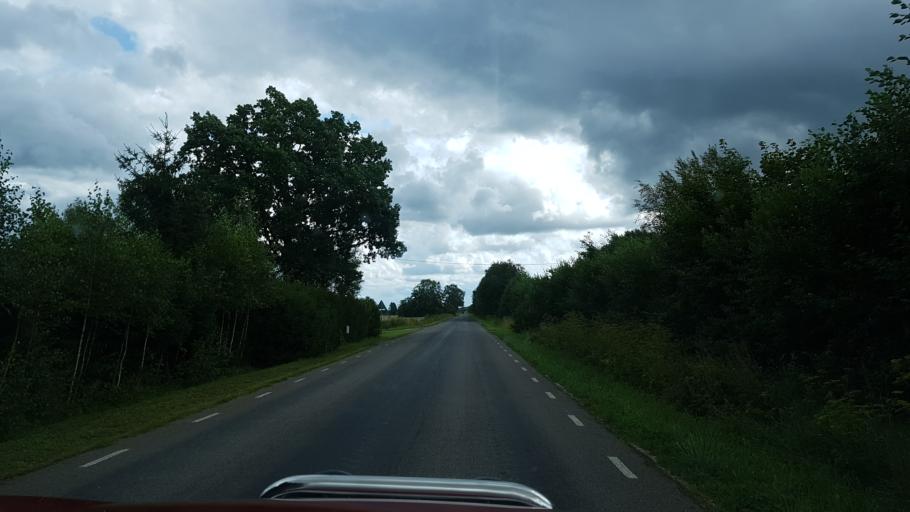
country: EE
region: Laeaene
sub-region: Lihula vald
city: Lihula
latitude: 58.7216
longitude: 23.9707
